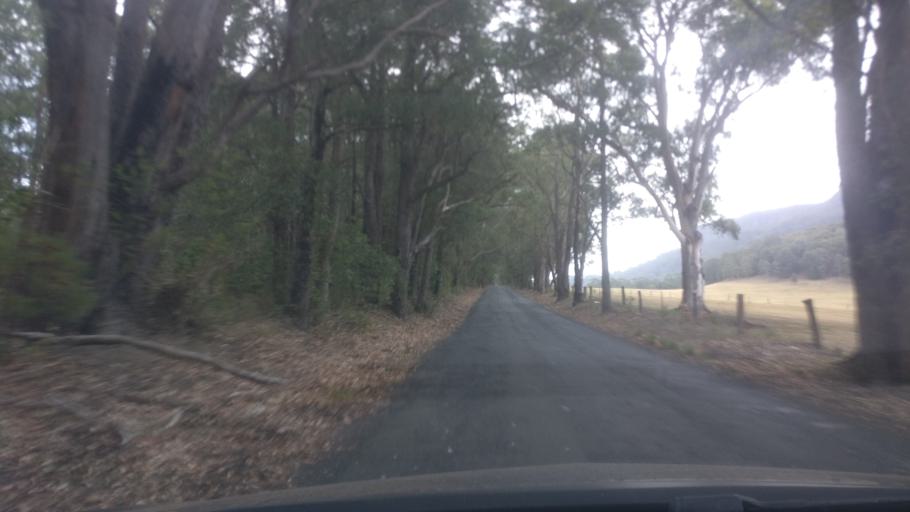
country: AU
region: New South Wales
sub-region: Shoalhaven Shire
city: Kangaroo Valley
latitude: -34.7214
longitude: 150.4716
